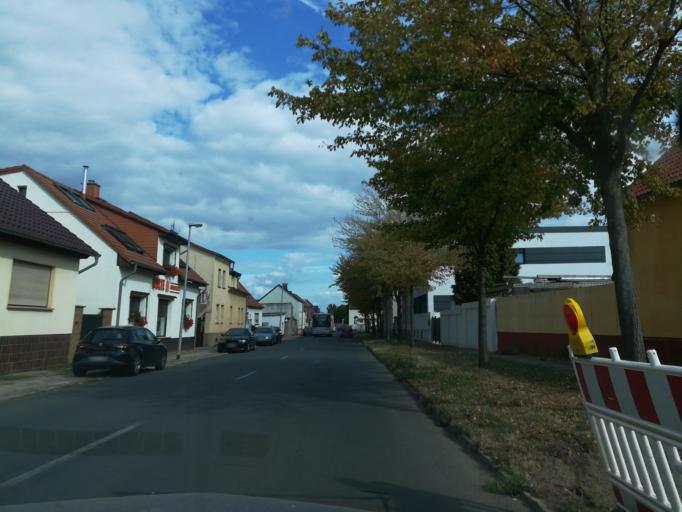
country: DE
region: Saxony-Anhalt
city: Diesdorf
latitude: 52.1322
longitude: 11.5690
